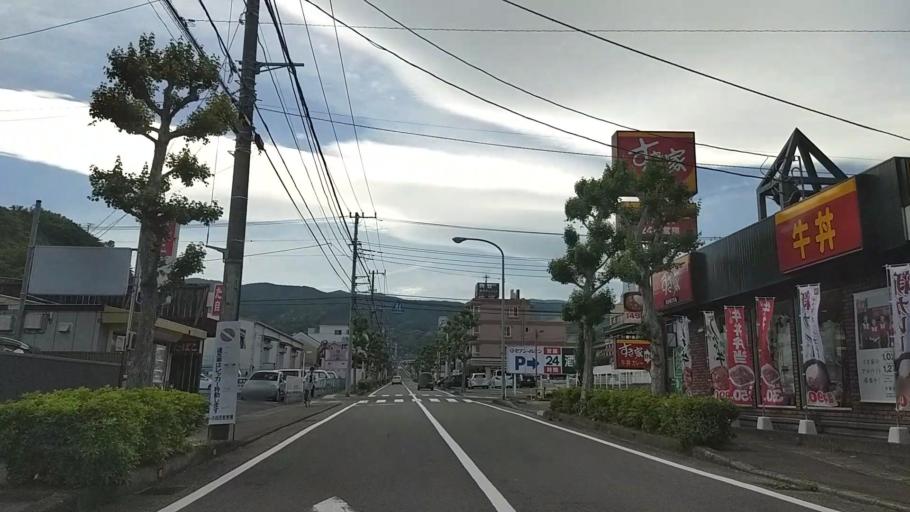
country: JP
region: Kanagawa
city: Odawara
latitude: 35.2439
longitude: 139.1389
